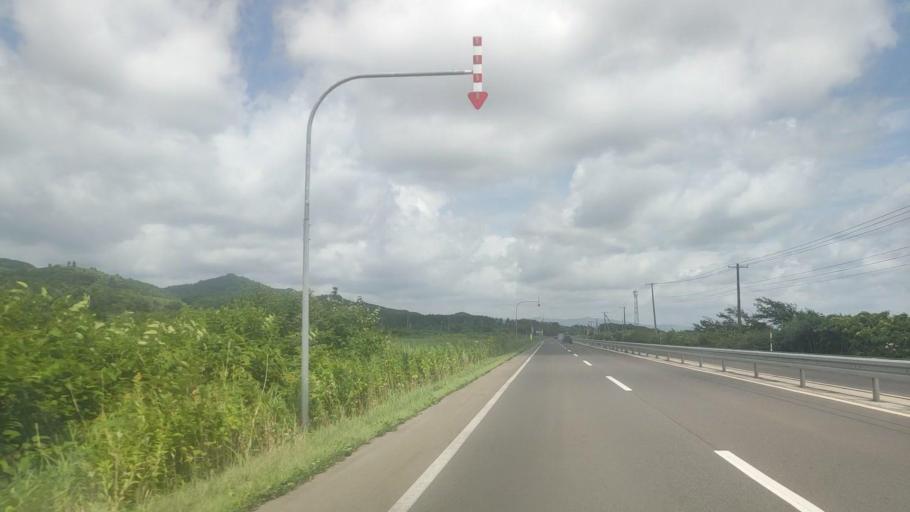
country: JP
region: Hokkaido
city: Niseko Town
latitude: 42.4514
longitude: 140.3315
